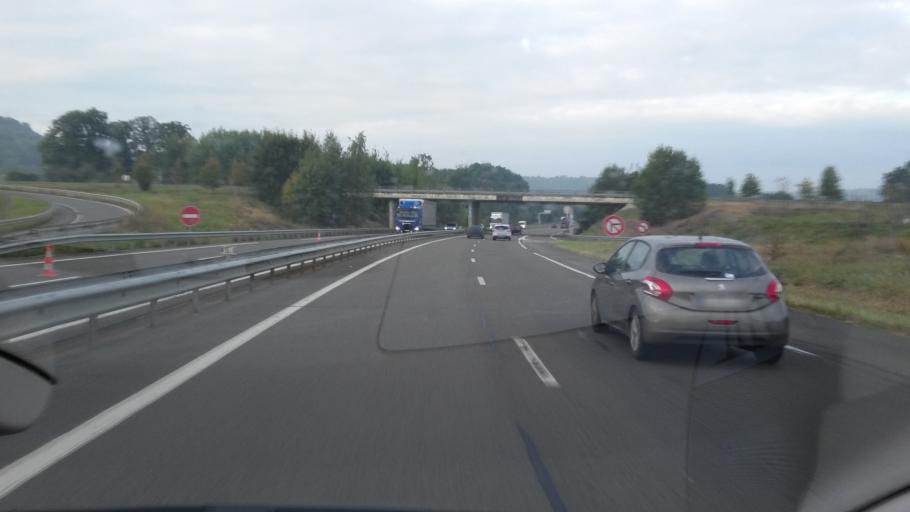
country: FR
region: Champagne-Ardenne
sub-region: Departement des Ardennes
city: La Francheville
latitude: 49.6436
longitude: 4.6279
